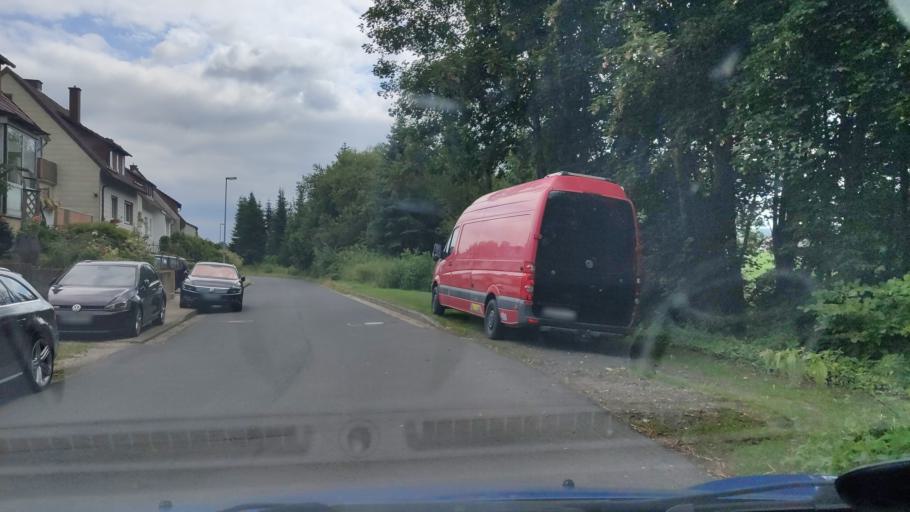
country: DE
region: Lower Saxony
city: Uslar
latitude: 51.6670
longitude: 9.6421
